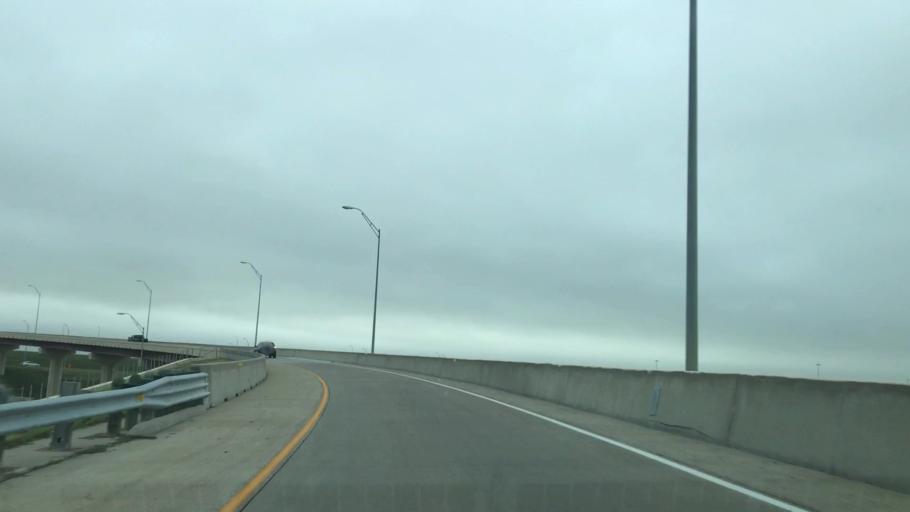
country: US
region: Texas
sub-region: Dallas County
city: Coppell
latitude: 32.9338
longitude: -97.0365
